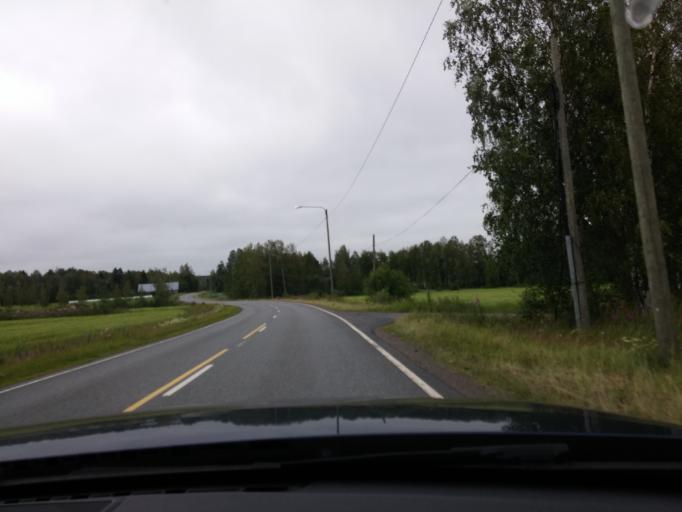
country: FI
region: Central Finland
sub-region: Joutsa
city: Joutsa
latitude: 61.8111
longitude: 25.9482
